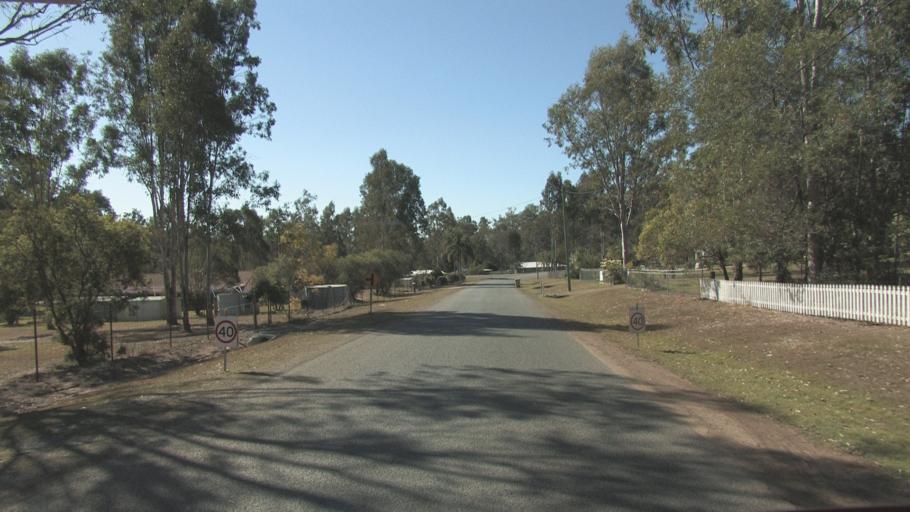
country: AU
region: Queensland
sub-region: Logan
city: Cedar Vale
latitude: -27.8532
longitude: 153.0161
